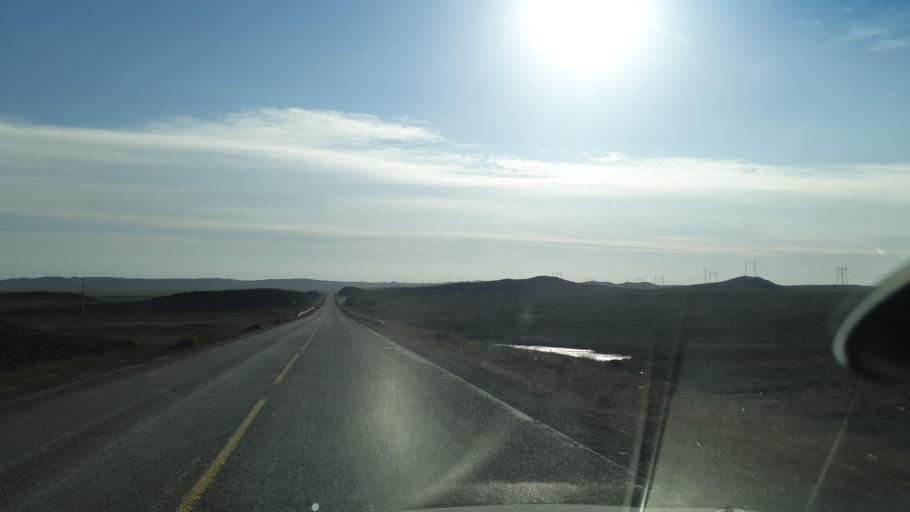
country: KZ
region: Zhambyl
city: Mynaral
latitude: 45.7025
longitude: 73.3990
